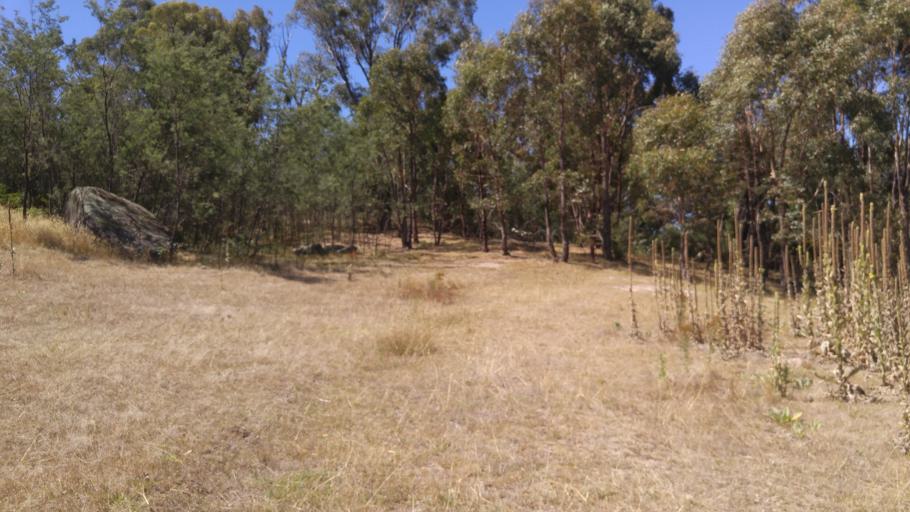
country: AU
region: Australian Capital Territory
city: Macarthur
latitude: -35.4495
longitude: 148.9258
